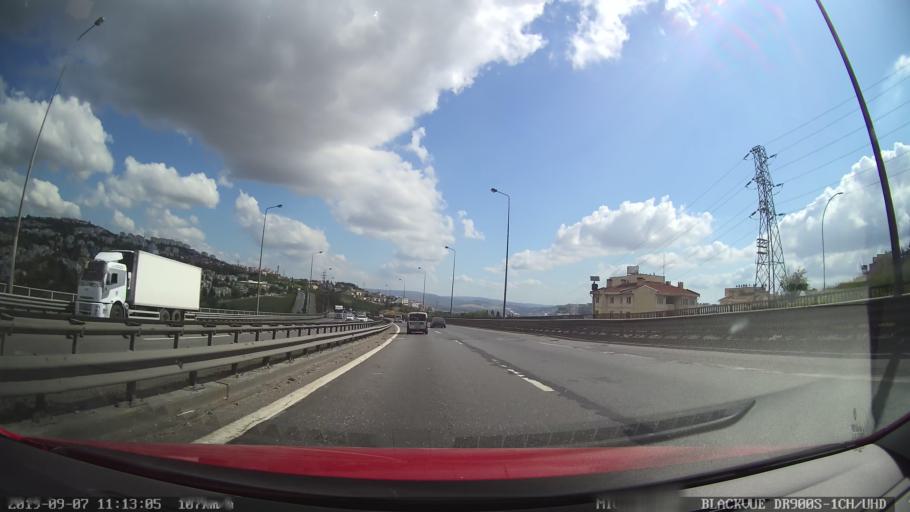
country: TR
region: Kocaeli
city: Izmit
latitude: 40.7817
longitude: 29.9405
